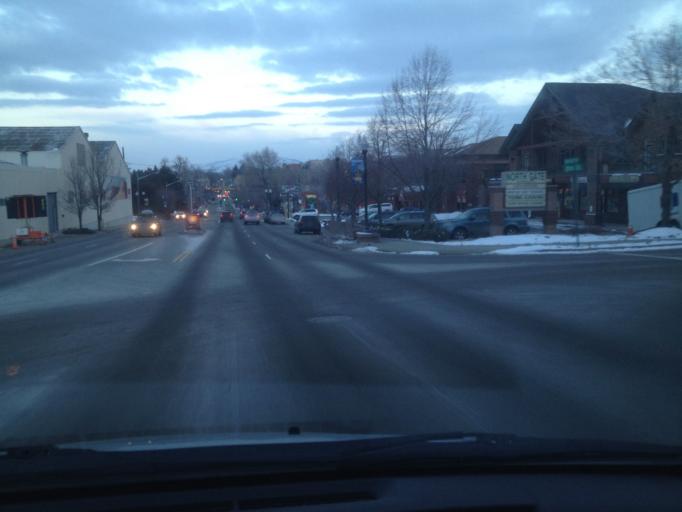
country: US
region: Colorado
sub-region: Jefferson County
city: Golden
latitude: 39.7593
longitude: -105.2250
